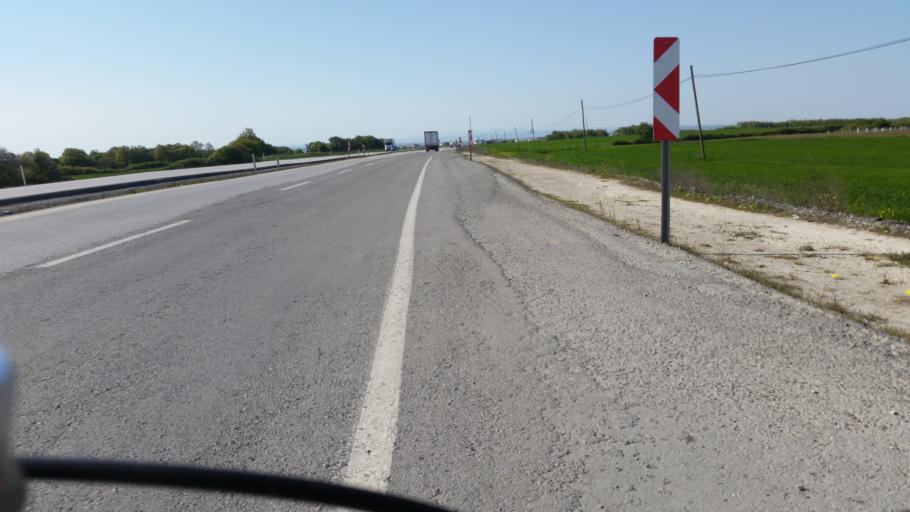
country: TR
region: Tekirdag
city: Cerkezkoey
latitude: 41.3433
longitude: 27.9632
